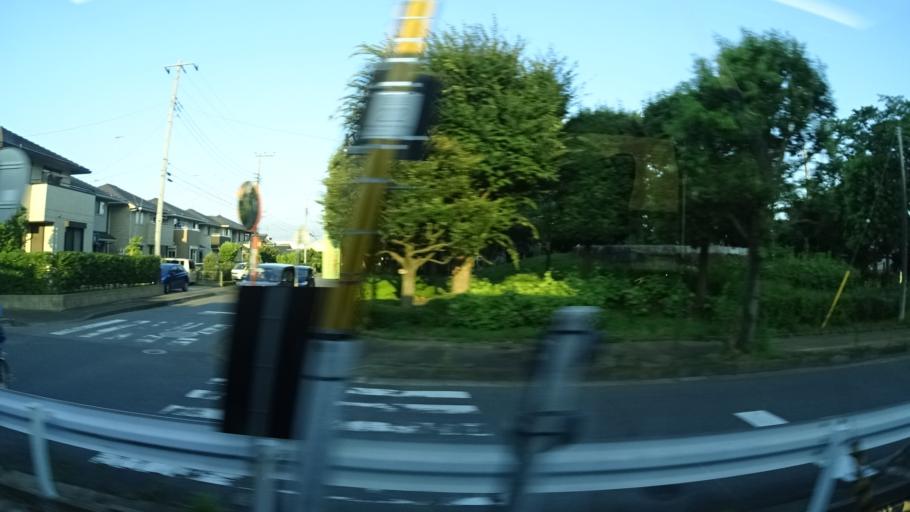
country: JP
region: Ibaraki
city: Ushiku
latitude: 35.9844
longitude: 140.1440
